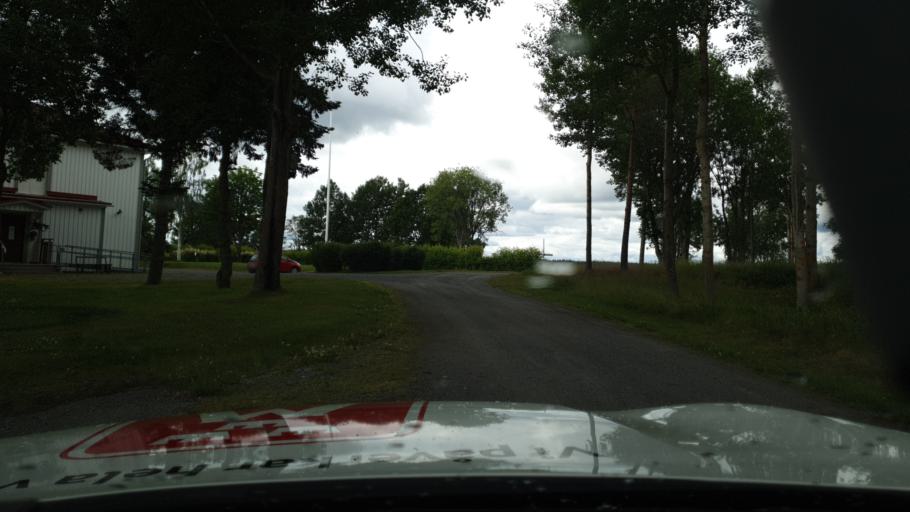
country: SE
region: Vaesterbotten
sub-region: Umea Kommun
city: Hoernefors
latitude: 63.6045
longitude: 19.9056
